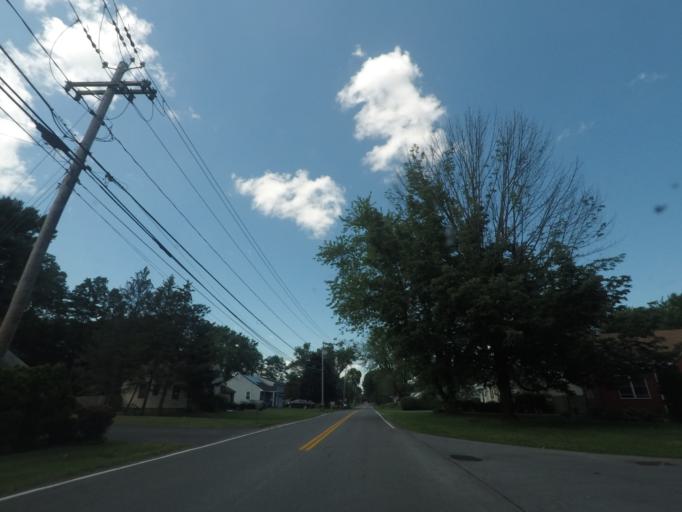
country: US
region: New York
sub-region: Schenectady County
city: Rotterdam
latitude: 42.7582
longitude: -73.9604
